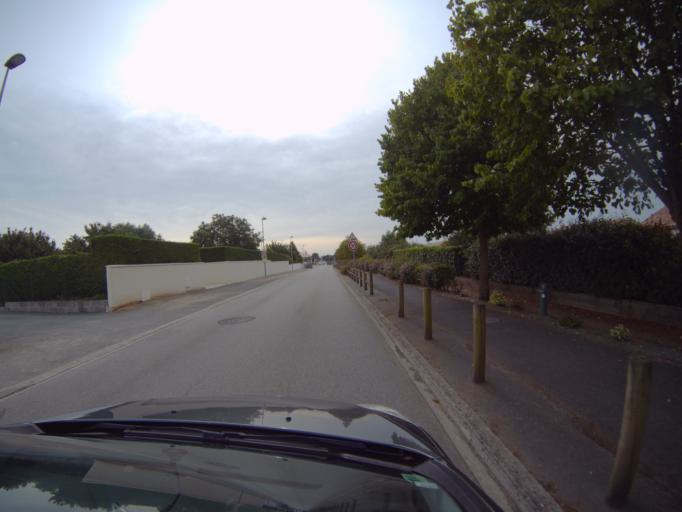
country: FR
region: Pays de la Loire
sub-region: Departement de la Vendee
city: Angles
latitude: 46.4070
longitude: -1.3967
